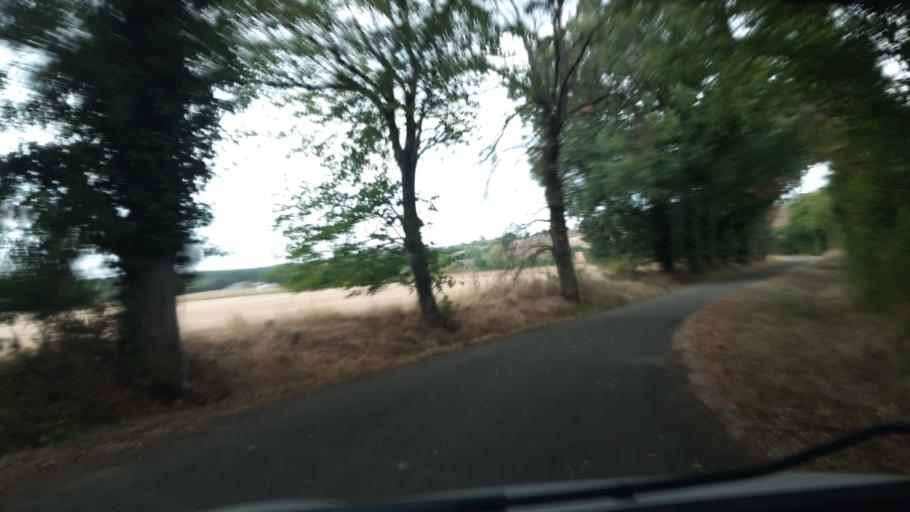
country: FR
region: Midi-Pyrenees
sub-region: Departement du Gers
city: Gimont
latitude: 43.6565
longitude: 0.9814
